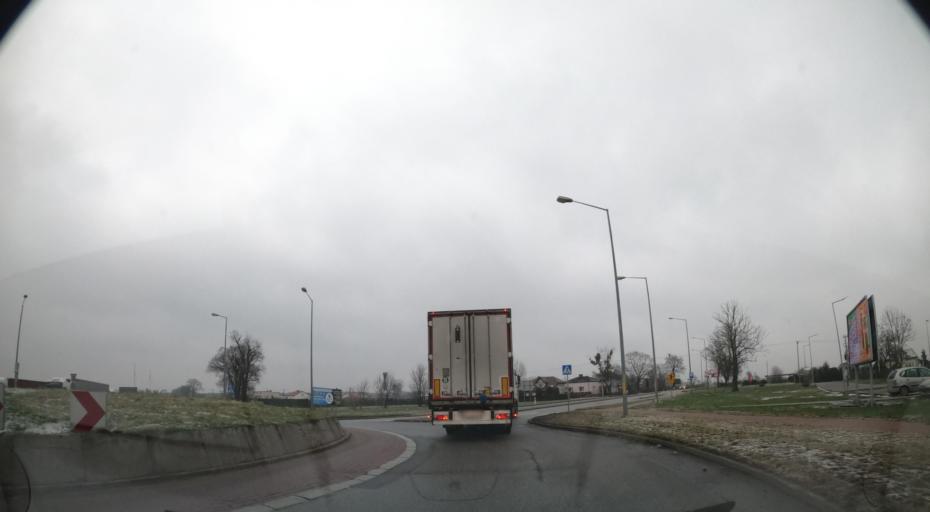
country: PL
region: Masovian Voivodeship
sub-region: Powiat sochaczewski
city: Mlodzieszyn
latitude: 52.2689
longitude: 20.1644
